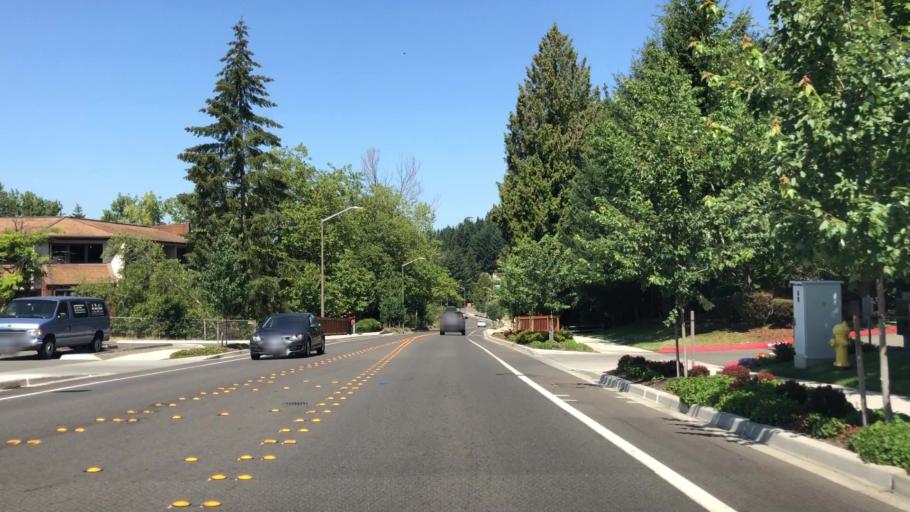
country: US
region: Washington
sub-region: King County
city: Yarrow Point
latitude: 47.6382
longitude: -122.1918
